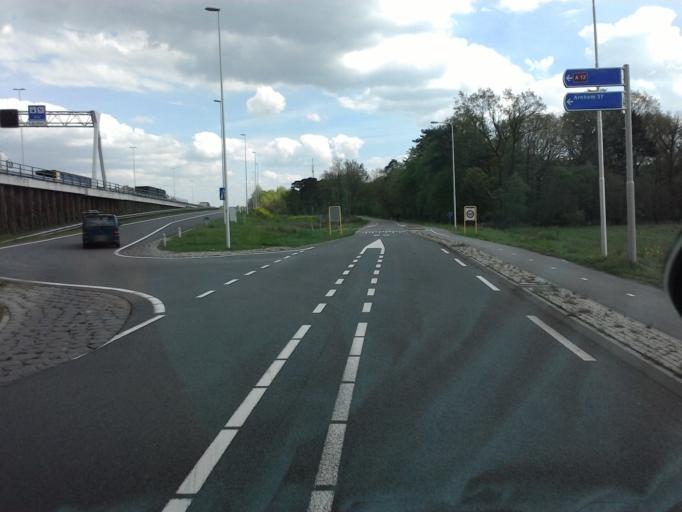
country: NL
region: Utrecht
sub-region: Gemeente Utrechtse Heuvelrug
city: Maarsbergen
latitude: 52.0541
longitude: 5.4044
